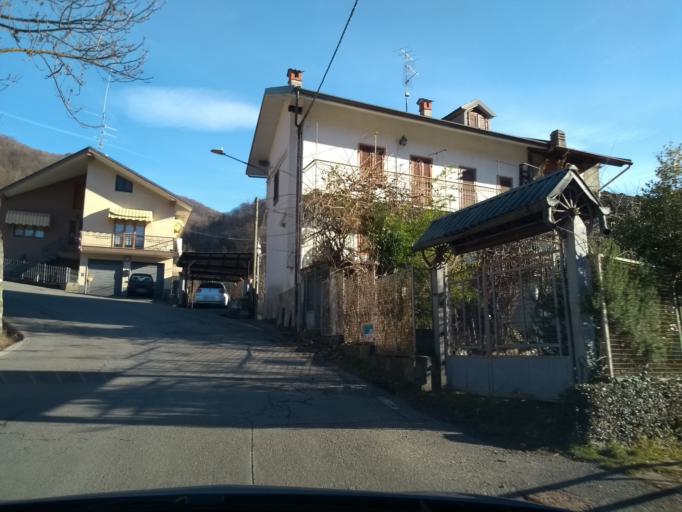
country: IT
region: Piedmont
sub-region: Provincia di Torino
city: Pessinetto
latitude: 45.2864
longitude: 7.4188
